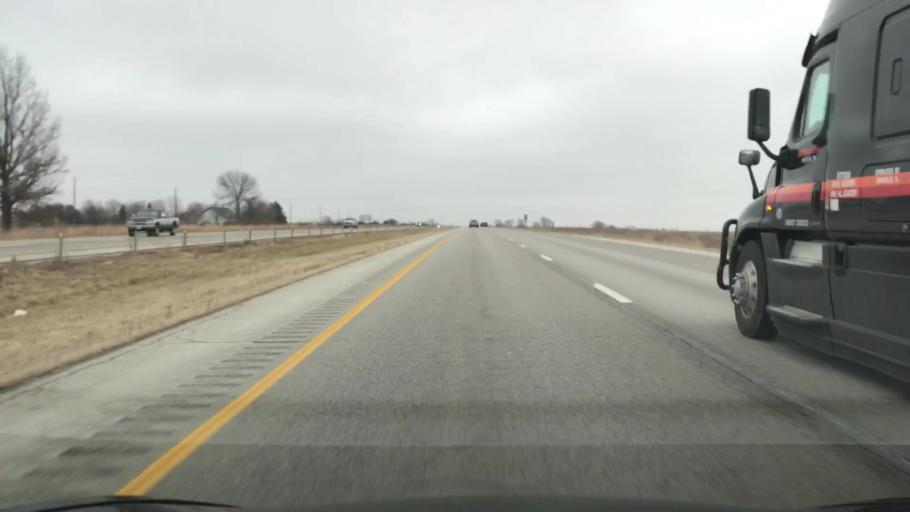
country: US
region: Iowa
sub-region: Madison County
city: Earlham
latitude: 41.5175
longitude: -94.1150
